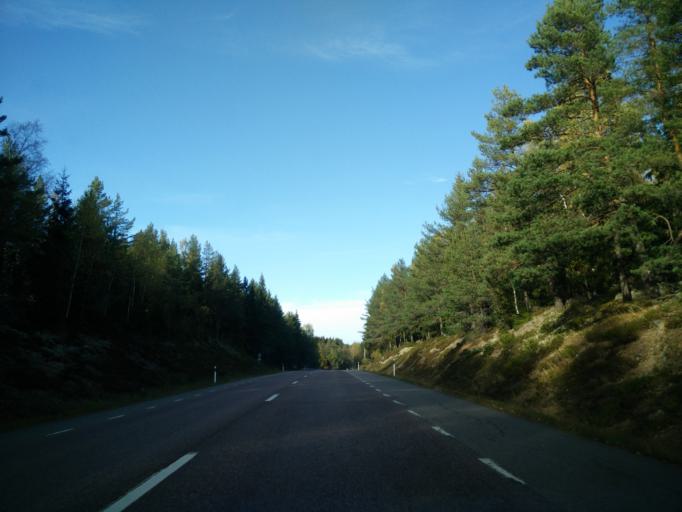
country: SE
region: Gaevleborg
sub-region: Hudiksvalls Kommun
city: Iggesund
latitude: 61.5868
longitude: 17.0258
